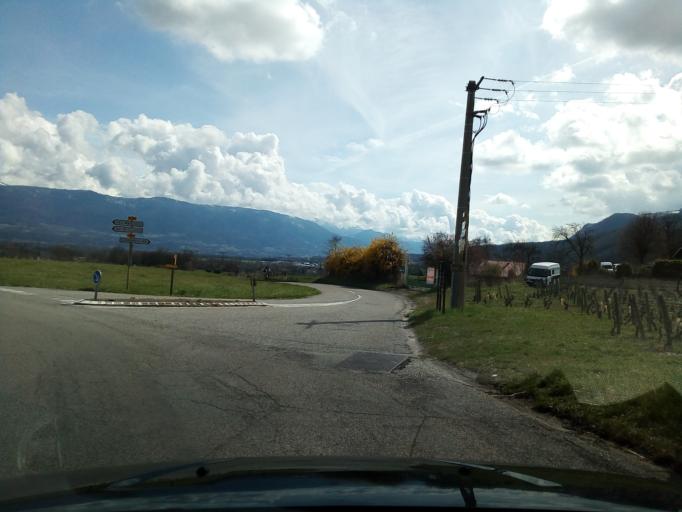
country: FR
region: Rhone-Alpes
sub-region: Departement de la Savoie
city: Les Marches
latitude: 45.4916
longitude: 5.9836
